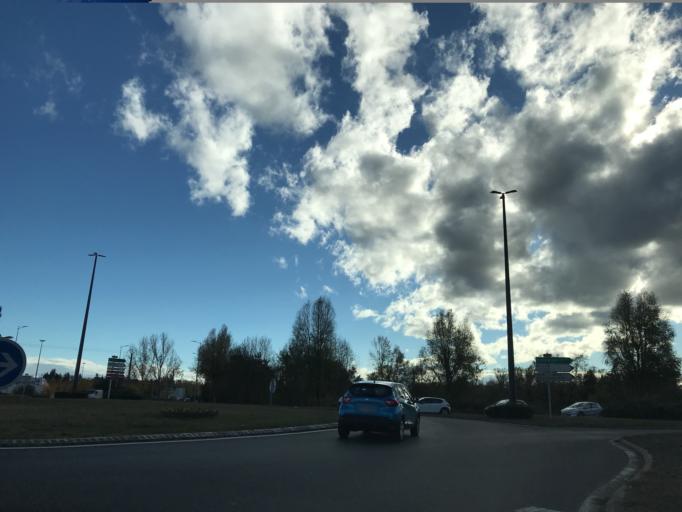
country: FR
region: Auvergne
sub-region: Departement du Puy-de-Dome
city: Peschadoires
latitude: 45.8407
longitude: 3.5060
